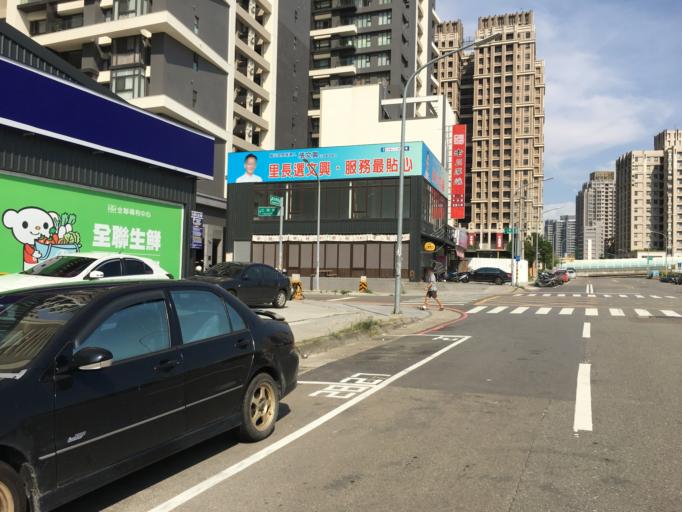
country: TW
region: Taiwan
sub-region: Hsinchu
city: Hsinchu
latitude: 24.7905
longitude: 121.0101
